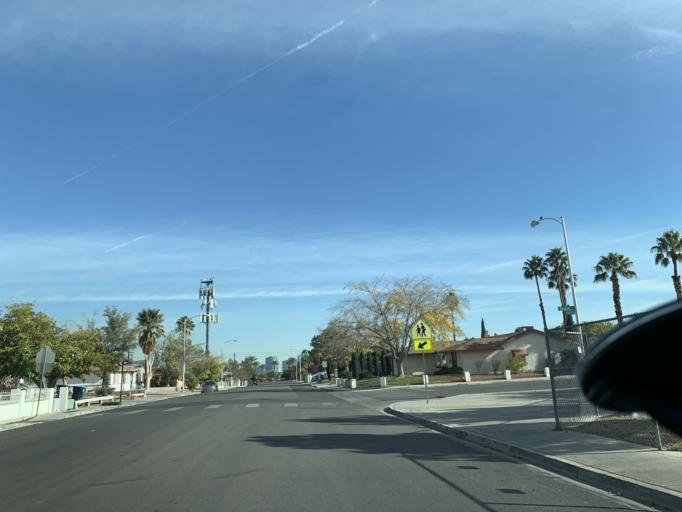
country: US
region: Nevada
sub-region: Clark County
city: Spring Valley
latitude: 36.1089
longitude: -115.2276
